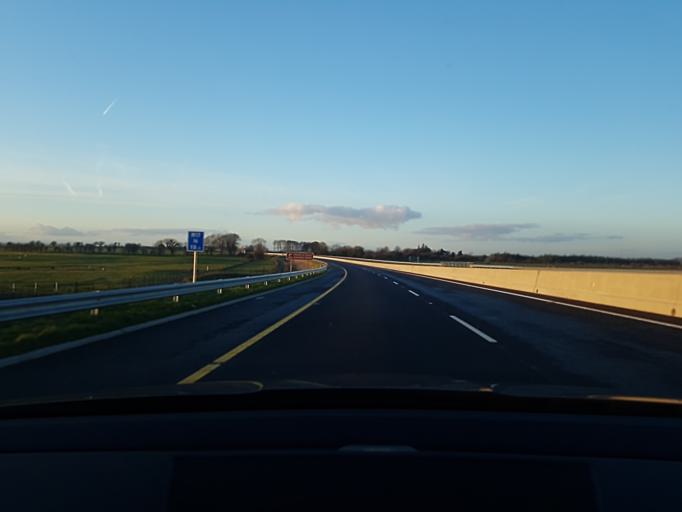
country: IE
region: Connaught
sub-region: County Galway
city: Tuam
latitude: 53.4589
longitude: -8.8488
